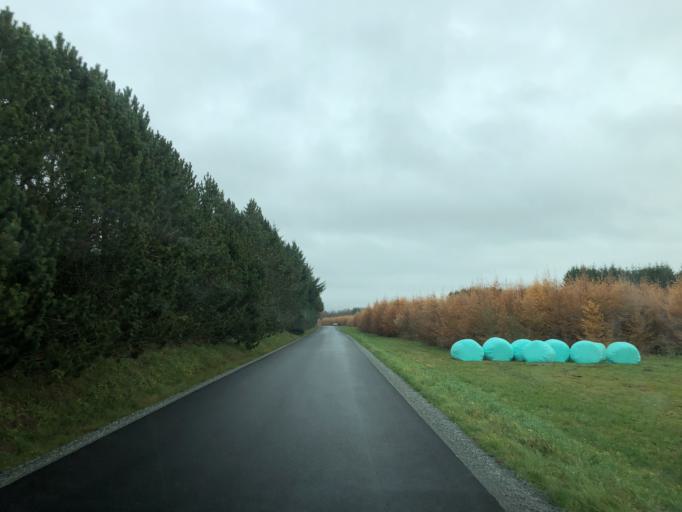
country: DK
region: Central Jutland
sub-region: Silkeborg Kommune
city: Virklund
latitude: 56.0695
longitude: 9.4995
